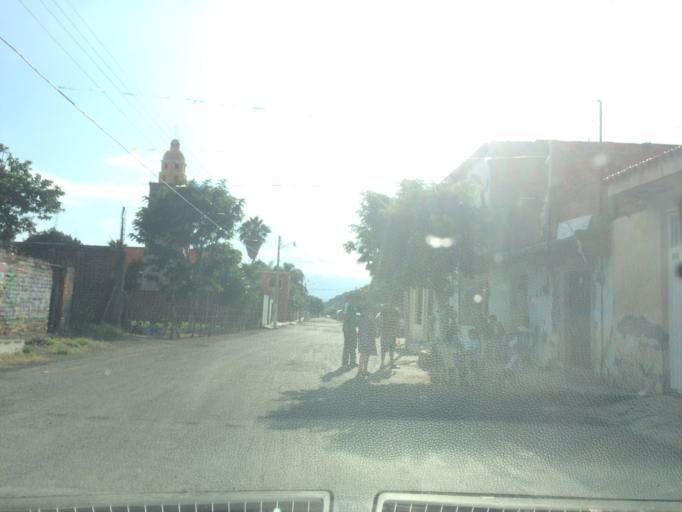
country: MX
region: Nayarit
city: Ixtlan del Rio
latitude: 21.0350
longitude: -104.3840
